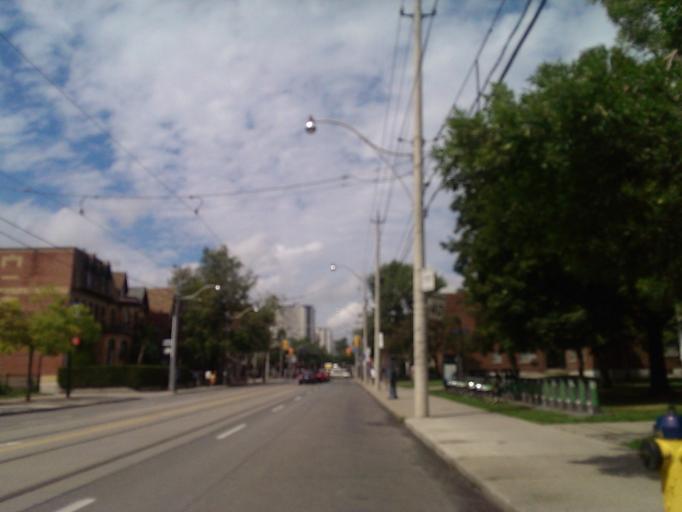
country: CA
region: Ontario
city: Toronto
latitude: 43.6609
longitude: -79.3665
